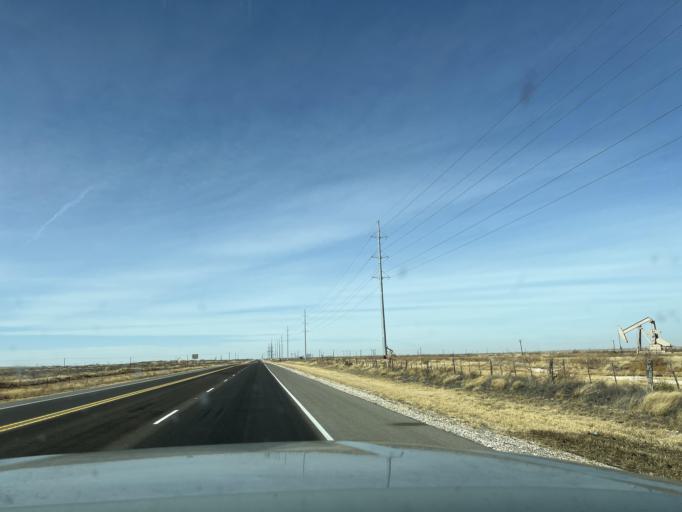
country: US
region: Texas
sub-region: Andrews County
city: Andrews
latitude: 32.3488
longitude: -102.7273
